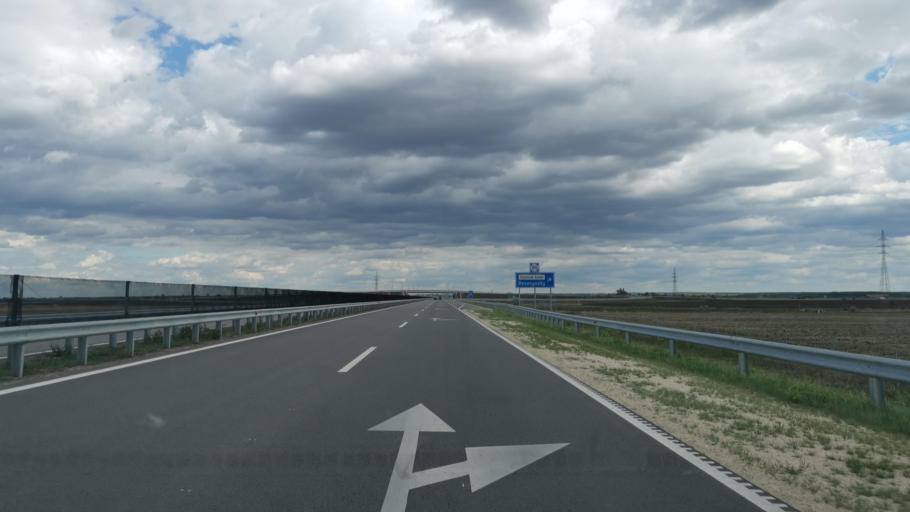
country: HU
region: Jasz-Nagykun-Szolnok
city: Szolnok
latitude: 47.2251
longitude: 20.2124
